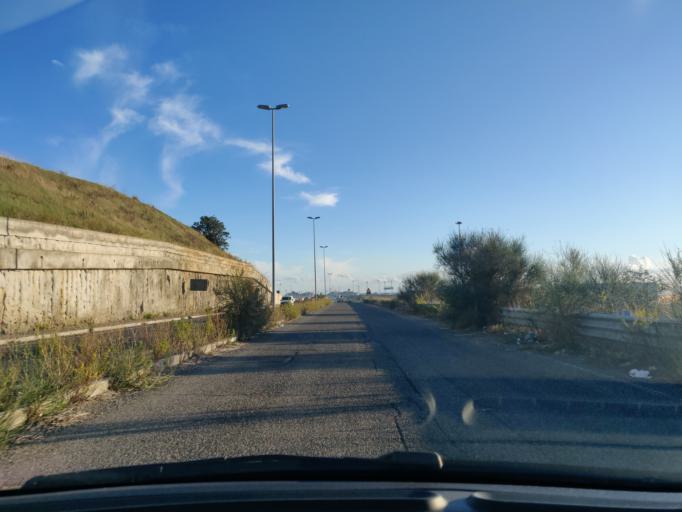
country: IT
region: Latium
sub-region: Citta metropolitana di Roma Capitale
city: Aurelia
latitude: 42.1266
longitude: 11.7780
